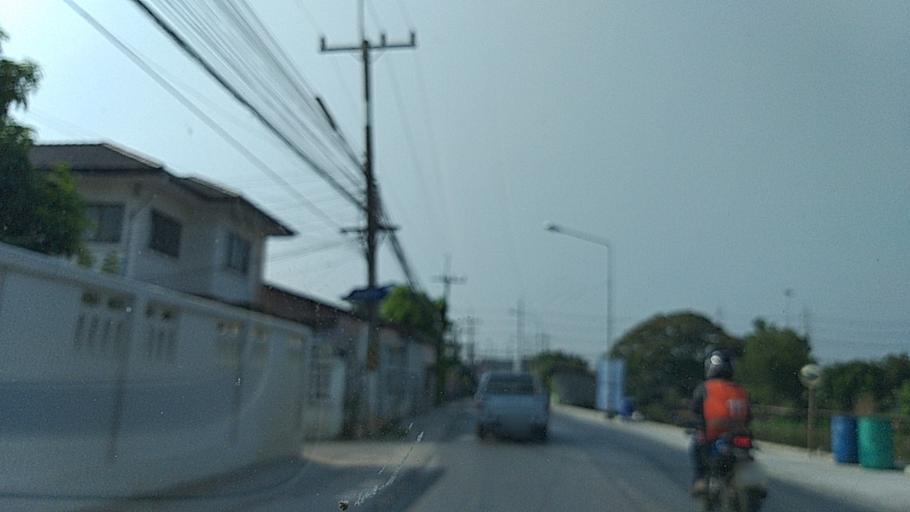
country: TH
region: Pathum Thani
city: Lam Luk Ka
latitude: 13.9354
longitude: 100.7061
